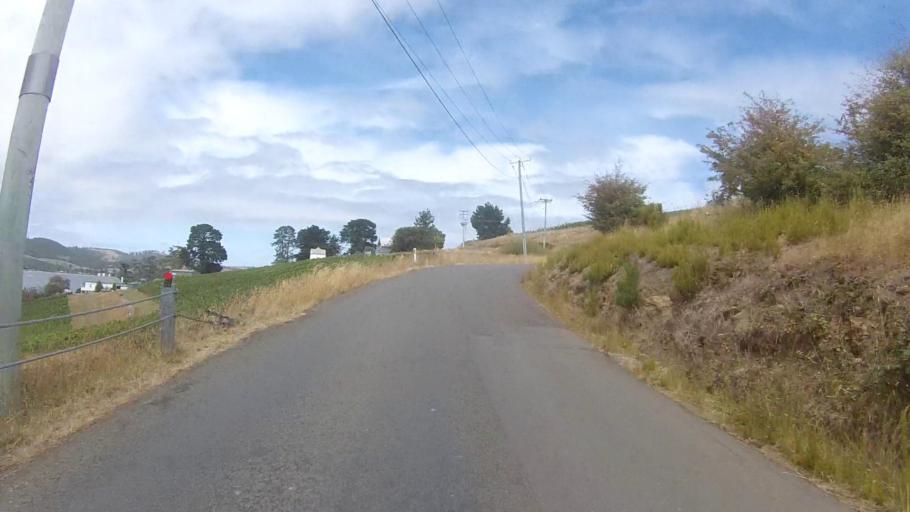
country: AU
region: Tasmania
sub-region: Kingborough
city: Blackmans Bay
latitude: -43.0554
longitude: 147.3275
